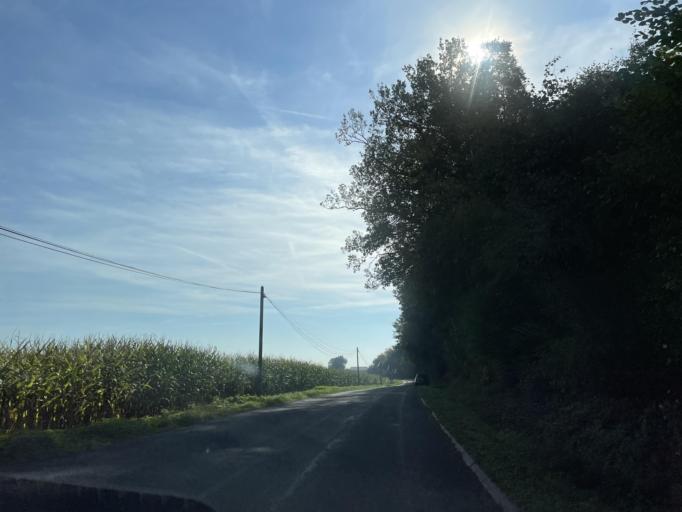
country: FR
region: Ile-de-France
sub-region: Departement de Seine-et-Marne
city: Saint-Jean-les-Deux-Jumeaux
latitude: 48.9103
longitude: 3.0207
